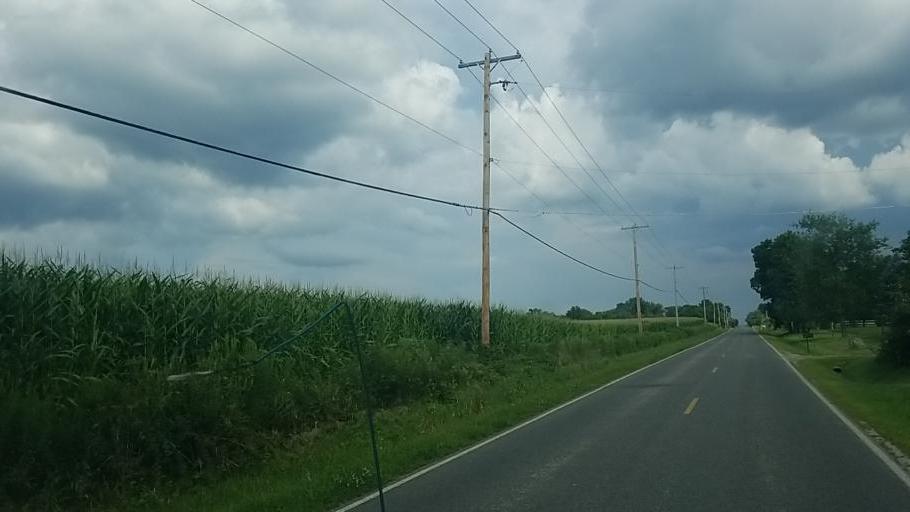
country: US
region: Ohio
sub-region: Medina County
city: Westfield Center
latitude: 41.0121
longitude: -81.9209
